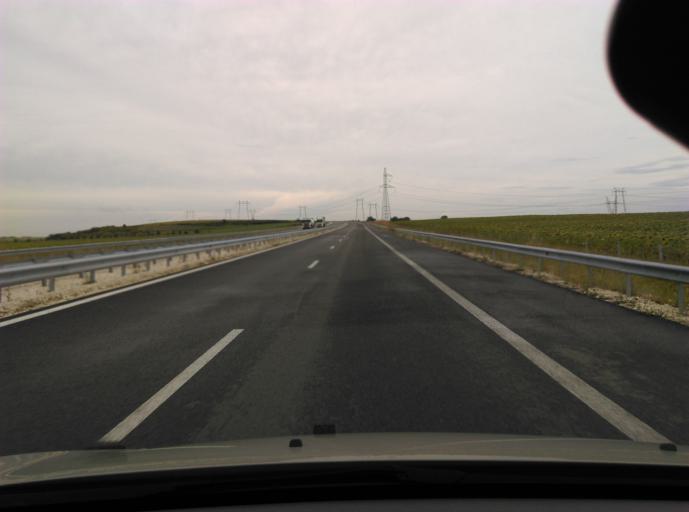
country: BG
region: Stara Zagora
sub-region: Obshtina Chirpan
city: Chirpan
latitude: 42.1256
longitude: 25.3701
